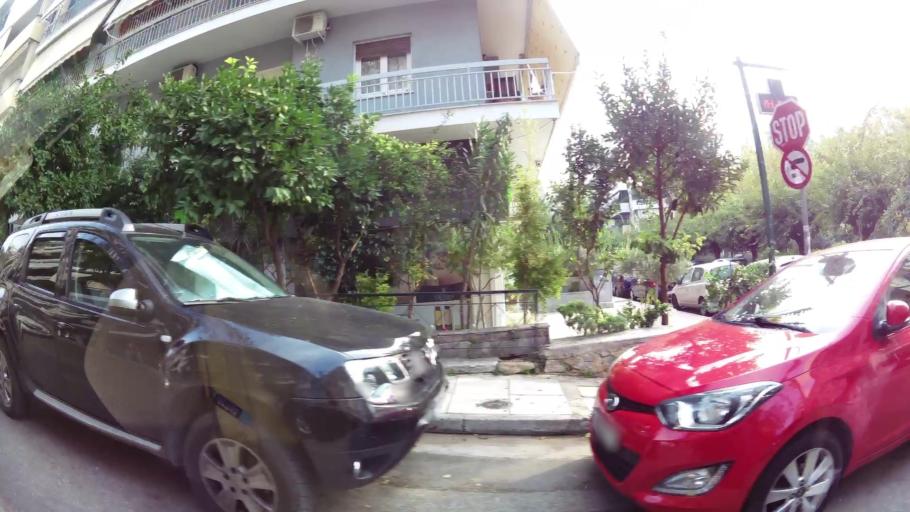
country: GR
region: Attica
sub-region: Nomarchia Athinas
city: Psychiko
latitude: 37.9948
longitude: 23.7631
